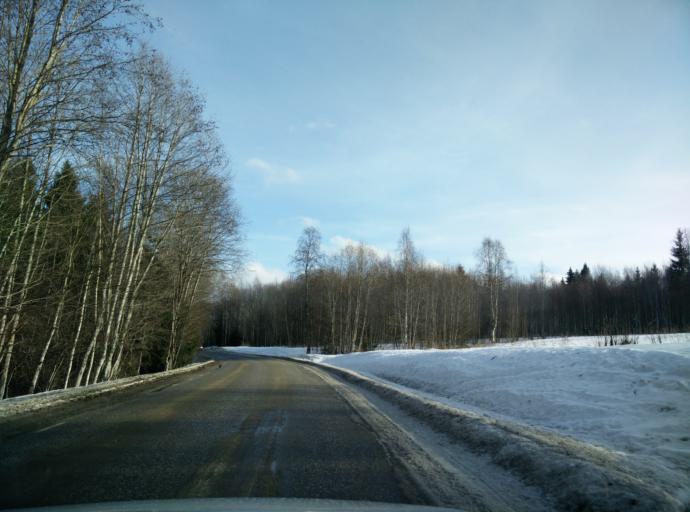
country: SE
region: Vaesternorrland
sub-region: Sundsvalls Kommun
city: Njurundabommen
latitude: 62.2206
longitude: 17.3528
